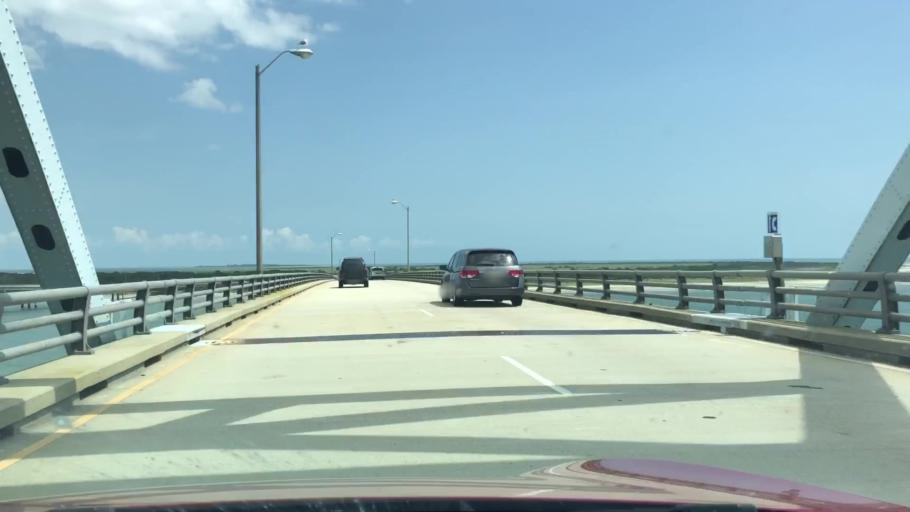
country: US
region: Virginia
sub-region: Northampton County
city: Cape Charles
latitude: 37.0892
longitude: -75.9845
